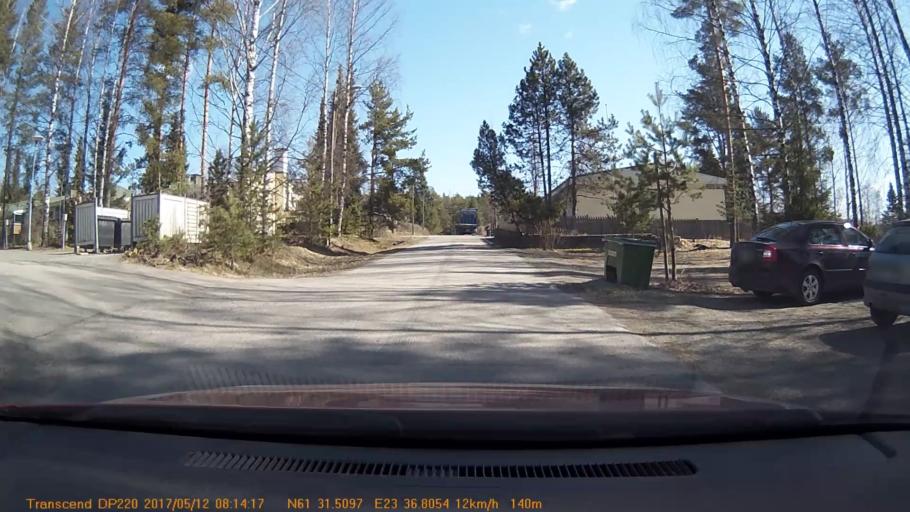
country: FI
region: Pirkanmaa
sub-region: Tampere
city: Yloejaervi
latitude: 61.5251
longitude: 23.6134
